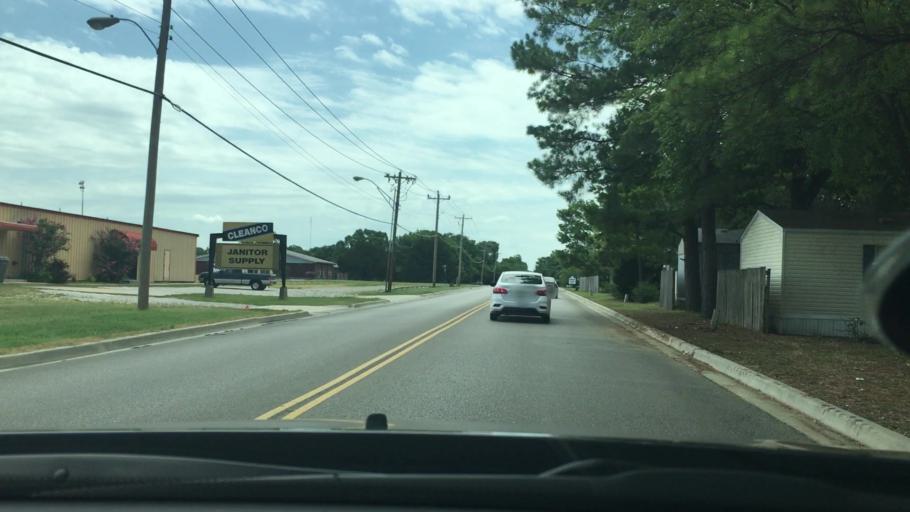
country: US
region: Oklahoma
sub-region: Carter County
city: Ardmore
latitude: 34.1802
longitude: -97.1555
